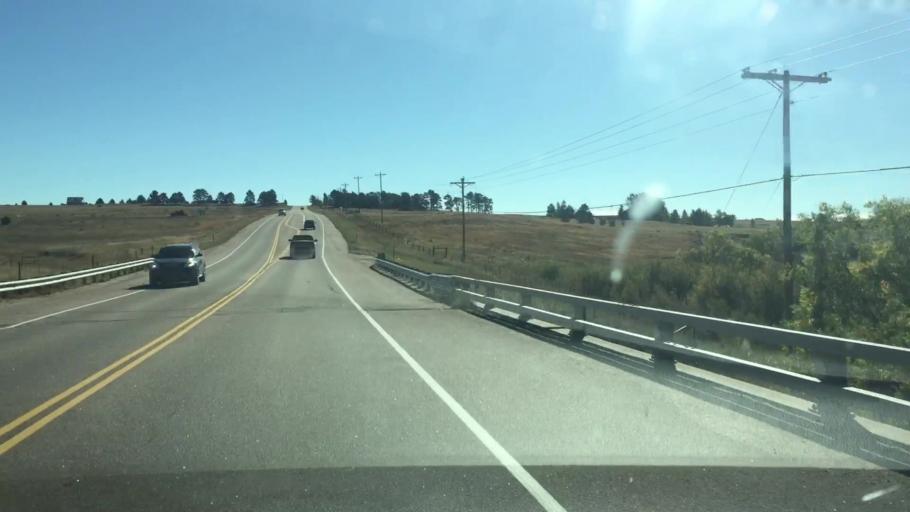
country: US
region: Colorado
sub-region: Elbert County
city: Elizabeth
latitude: 39.3588
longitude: -104.5351
